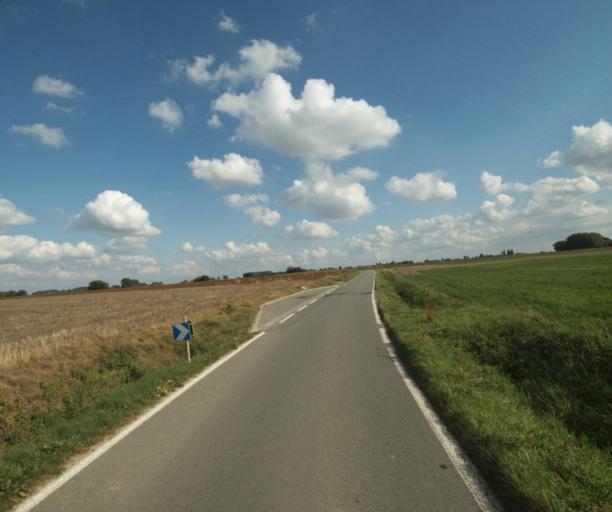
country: FR
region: Nord-Pas-de-Calais
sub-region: Departement du Nord
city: Fournes-en-Weppes
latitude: 50.5728
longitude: 2.8759
